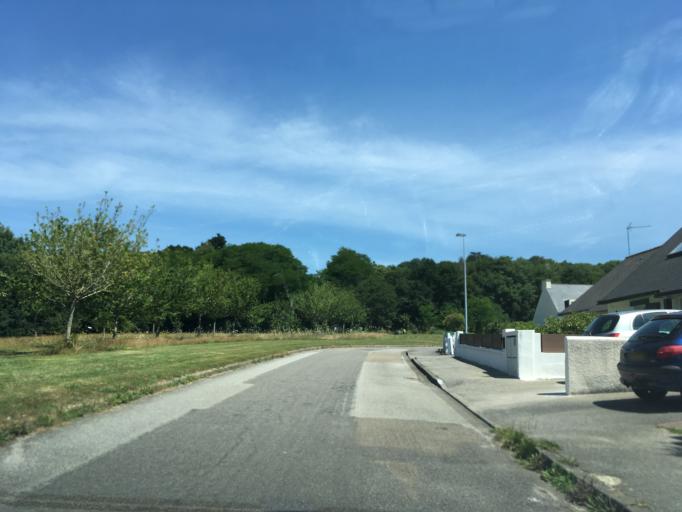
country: FR
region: Brittany
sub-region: Departement du Finistere
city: Quimper
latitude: 48.0065
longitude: -4.1141
